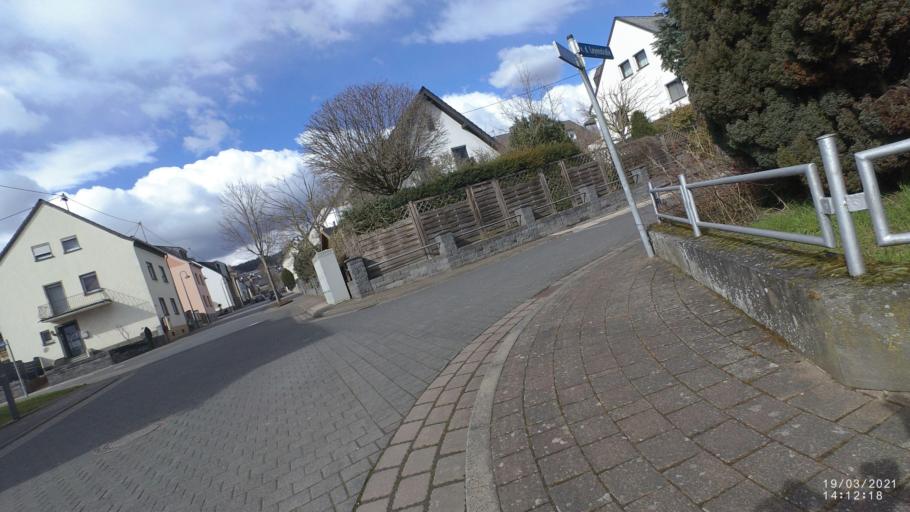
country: DE
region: Rheinland-Pfalz
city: Nickenich
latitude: 50.4109
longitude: 7.3317
